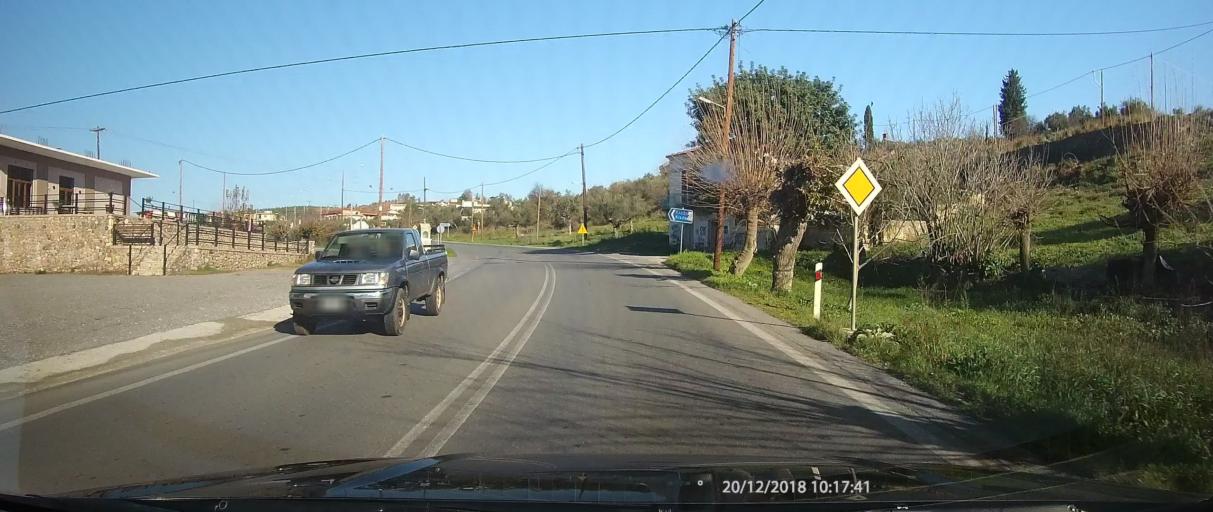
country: GR
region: Peloponnese
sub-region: Nomos Lakonias
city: Sparti
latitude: 37.1097
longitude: 22.4339
